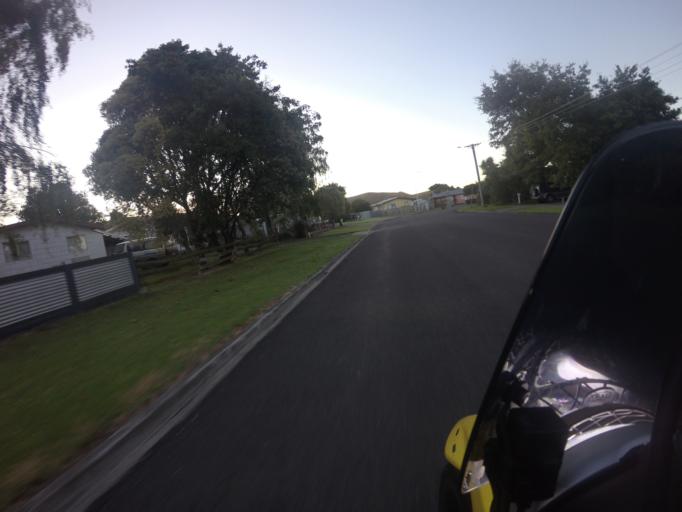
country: NZ
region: Gisborne
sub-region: Gisborne District
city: Gisborne
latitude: -38.6847
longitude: 178.0582
